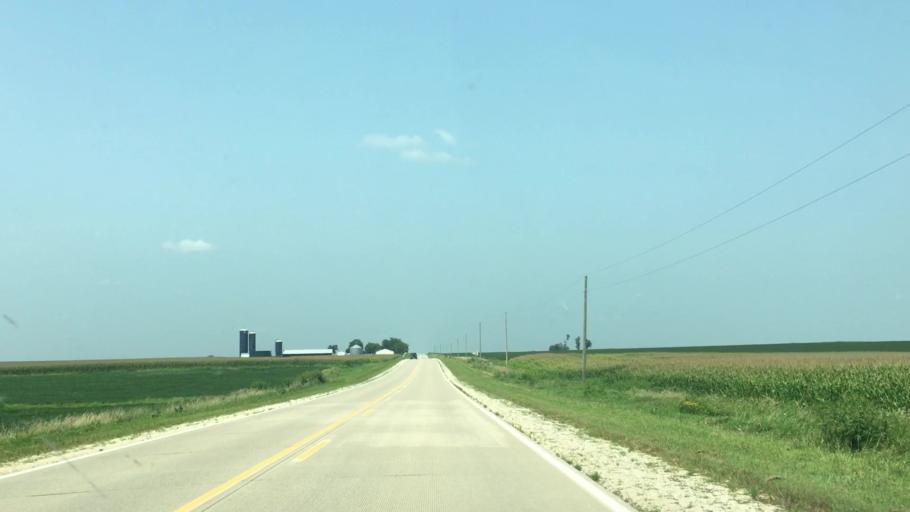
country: US
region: Iowa
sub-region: Fayette County
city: Fayette
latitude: 42.7363
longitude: -91.8040
